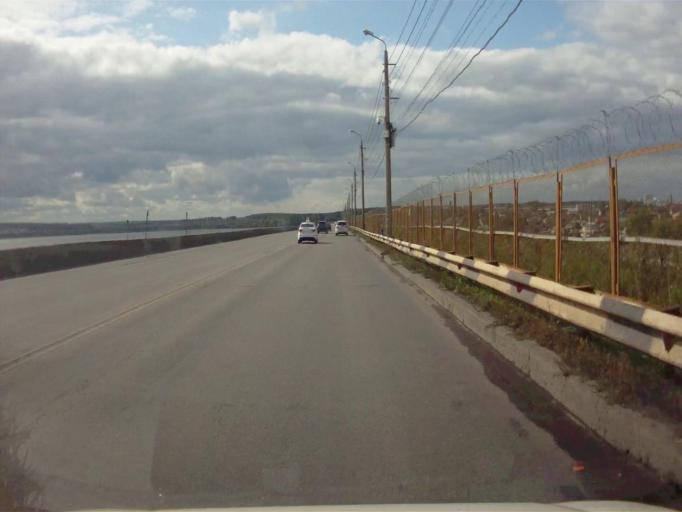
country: RU
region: Chelyabinsk
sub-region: Gorod Chelyabinsk
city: Chelyabinsk
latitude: 55.1459
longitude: 61.3207
